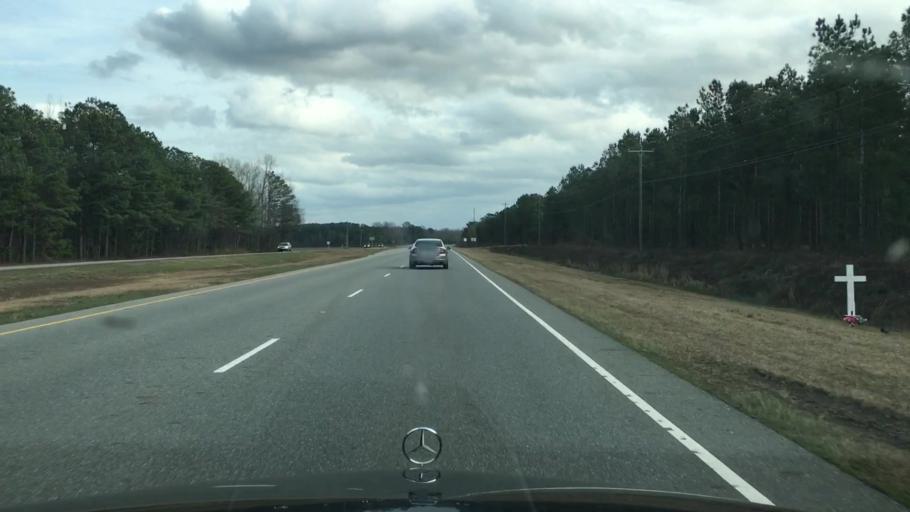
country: US
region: North Carolina
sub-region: Duplin County
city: Kenansville
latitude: 34.9498
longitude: -77.8886
